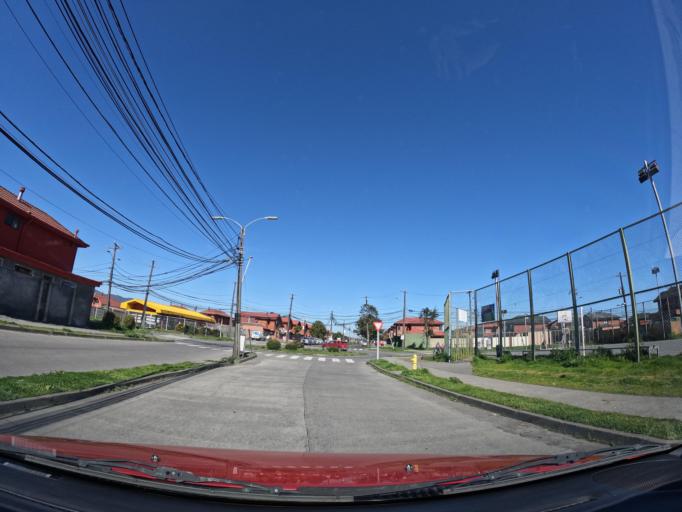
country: CL
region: Biobio
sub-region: Provincia de Concepcion
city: Concepcion
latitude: -36.8856
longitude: -73.1455
